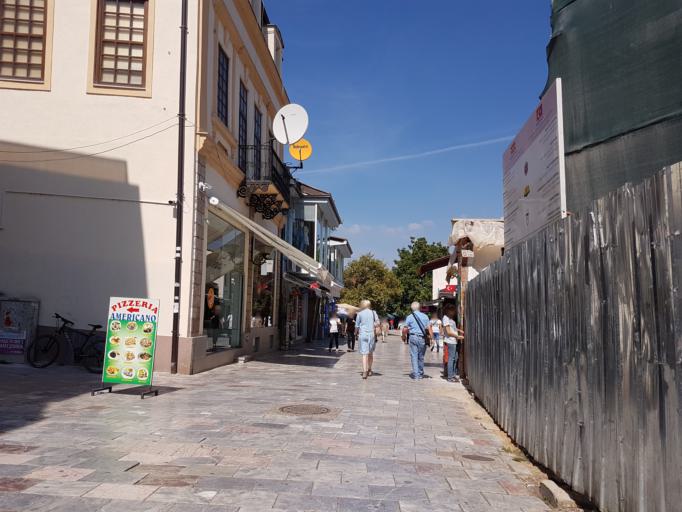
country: MK
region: Ohrid
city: Ohrid
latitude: 41.1153
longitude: 20.8004
